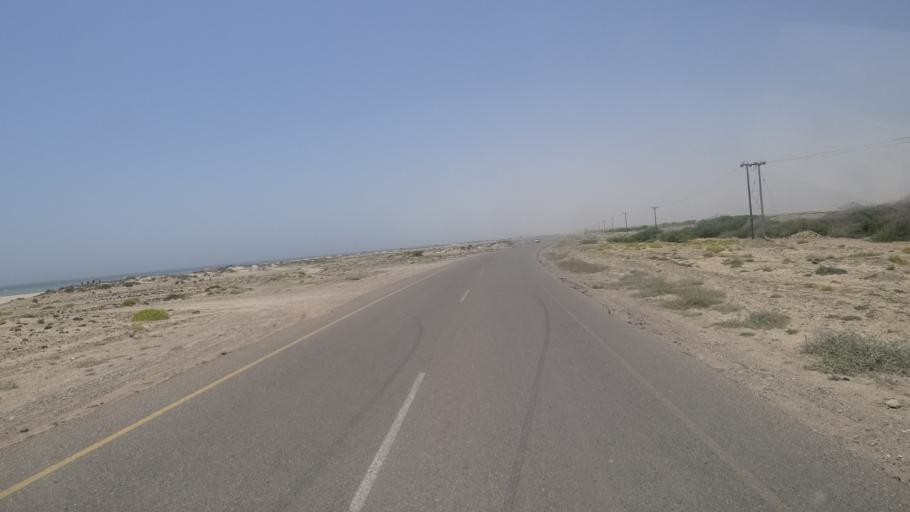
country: OM
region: Ash Sharqiyah
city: Sur
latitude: 22.1046
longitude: 59.7059
